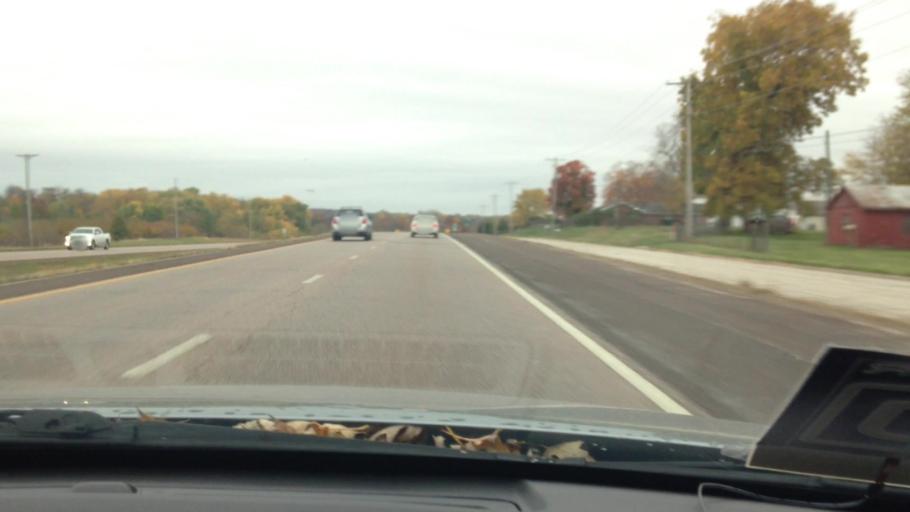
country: US
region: Kansas
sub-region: Leavenworth County
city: Basehor
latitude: 39.1500
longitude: -94.9010
